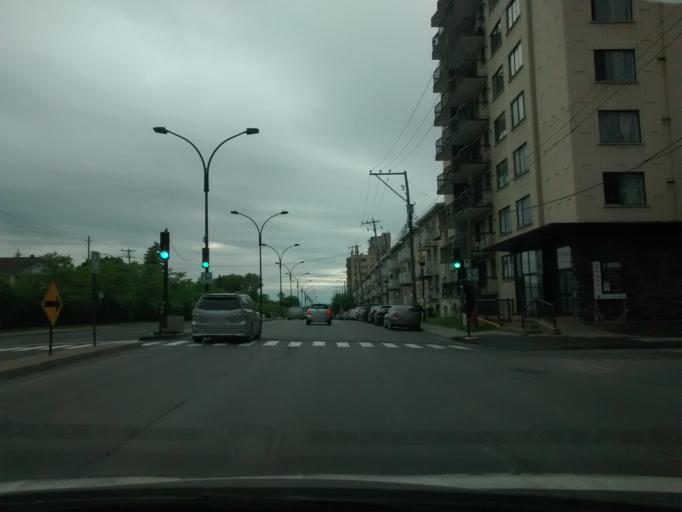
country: CA
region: Quebec
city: Mont-Royal
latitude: 45.5284
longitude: -73.6406
